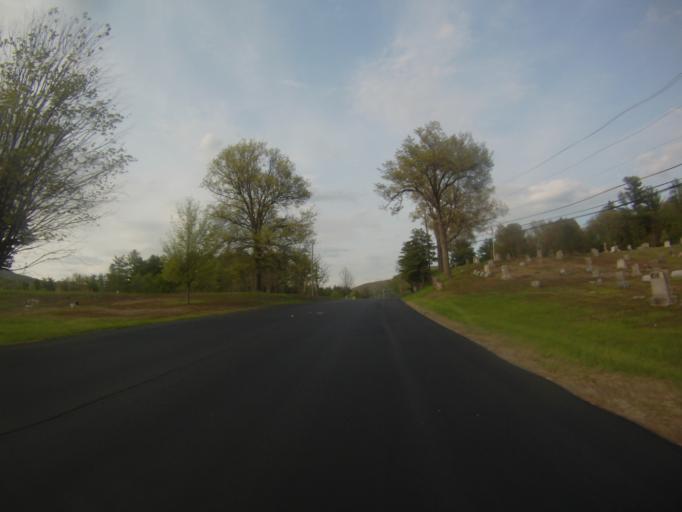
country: US
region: New York
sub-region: Essex County
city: Ticonderoga
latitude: 43.8118
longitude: -73.4870
